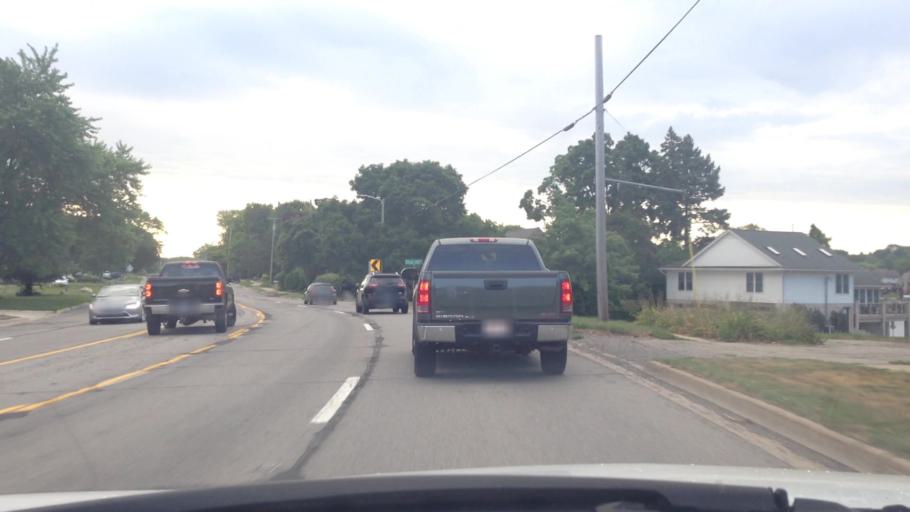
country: US
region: Michigan
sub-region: Oakland County
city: Pontiac
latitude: 42.6806
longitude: -83.3394
